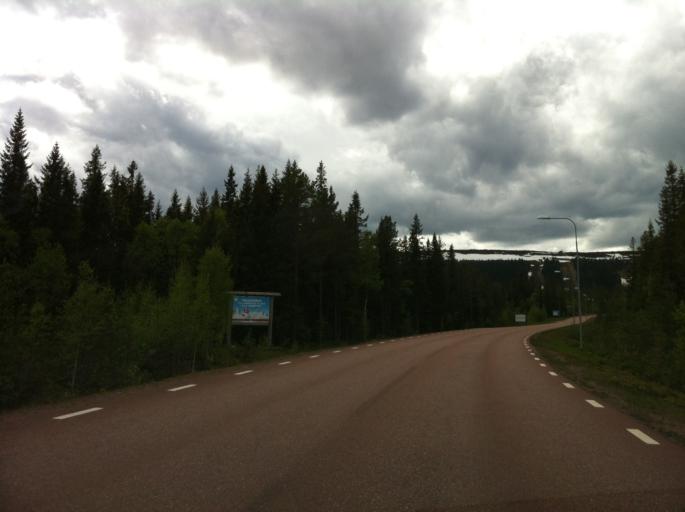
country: SE
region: Dalarna
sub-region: Malung-Saelens kommun
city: Malung
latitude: 61.1552
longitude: 13.2677
